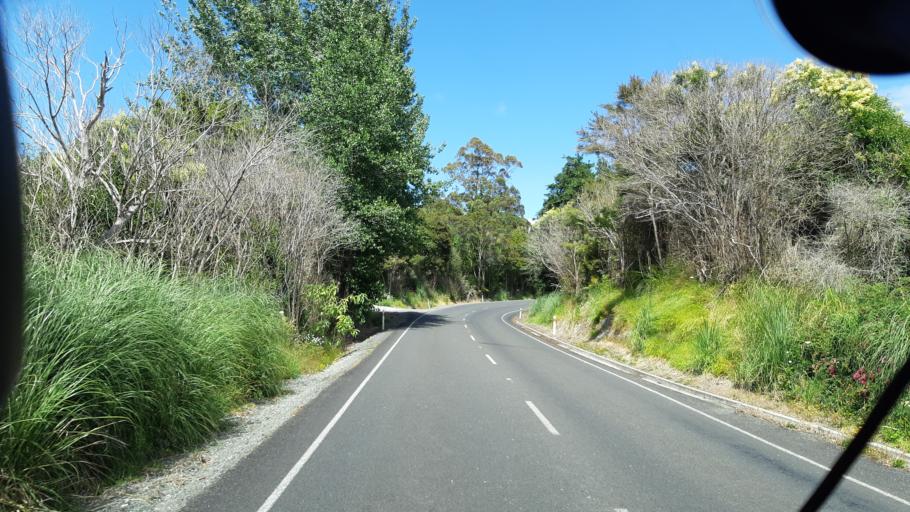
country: NZ
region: Northland
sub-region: Far North District
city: Taipa
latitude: -35.2668
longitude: 173.4997
